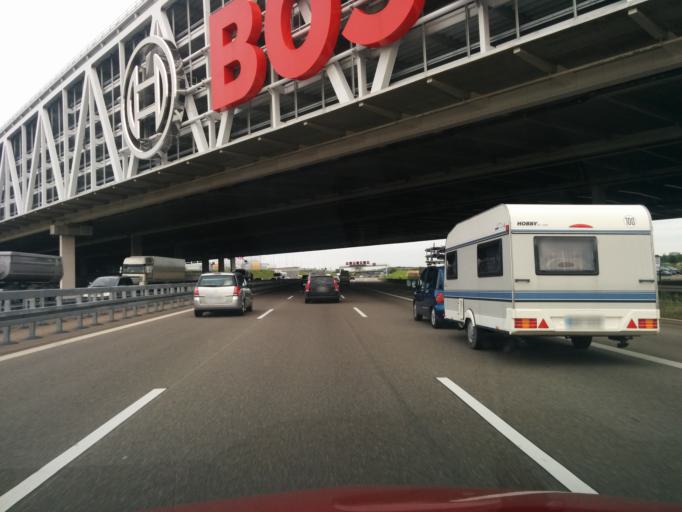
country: DE
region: Baden-Wuerttemberg
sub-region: Regierungsbezirk Stuttgart
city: Leinfelden-Echterdingen
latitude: 48.6945
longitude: 9.1959
